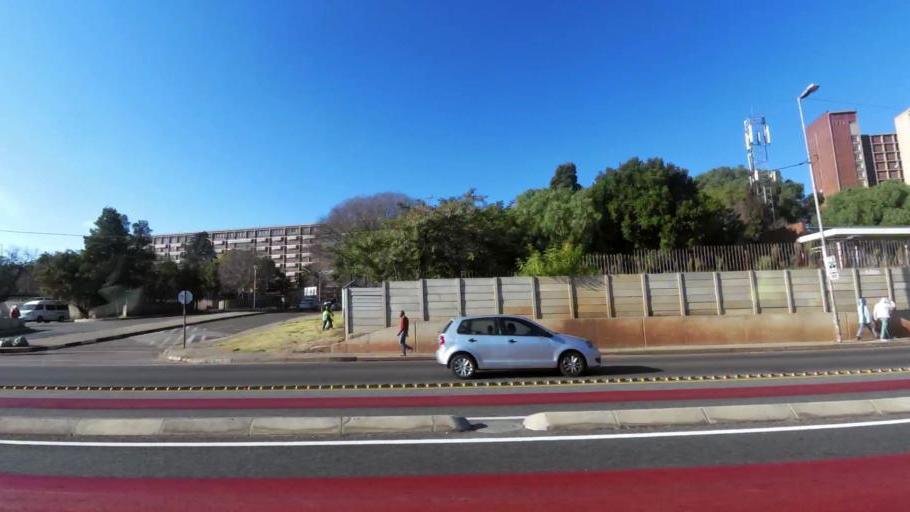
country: ZA
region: Gauteng
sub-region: City of Johannesburg Metropolitan Municipality
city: Johannesburg
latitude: -26.1842
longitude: 27.9881
